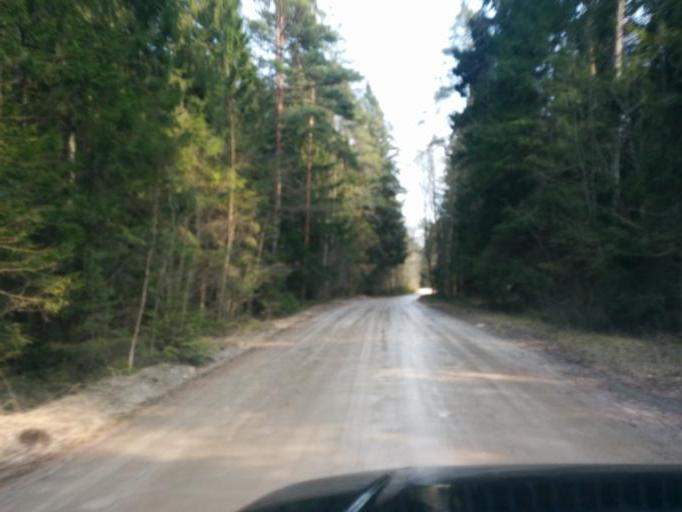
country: LV
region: Olaine
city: Olaine
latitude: 56.7910
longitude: 24.0242
